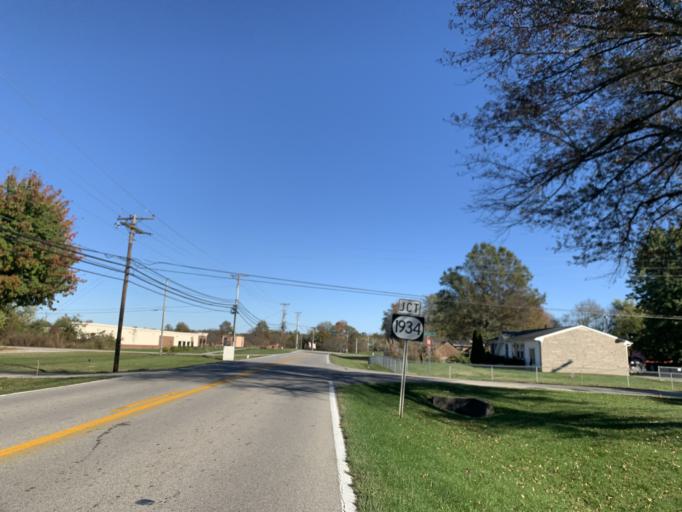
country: US
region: Kentucky
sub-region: Jefferson County
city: Pleasure Ridge Park
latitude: 38.1474
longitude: -85.8899
